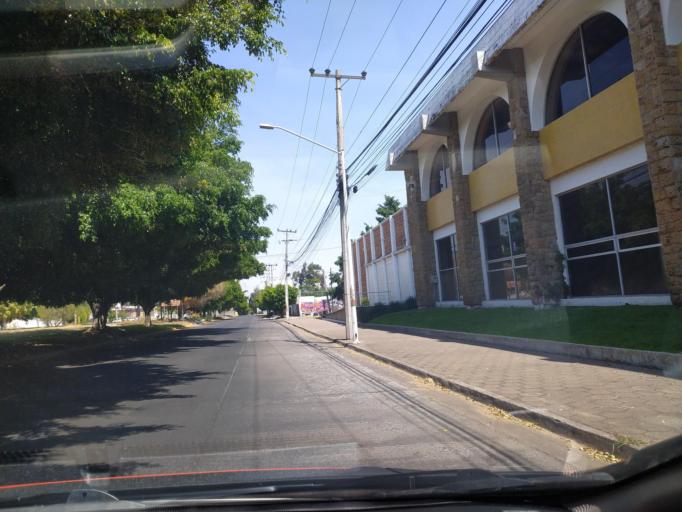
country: MX
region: Jalisco
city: Guadalajara
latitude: 20.6712
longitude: -103.3915
